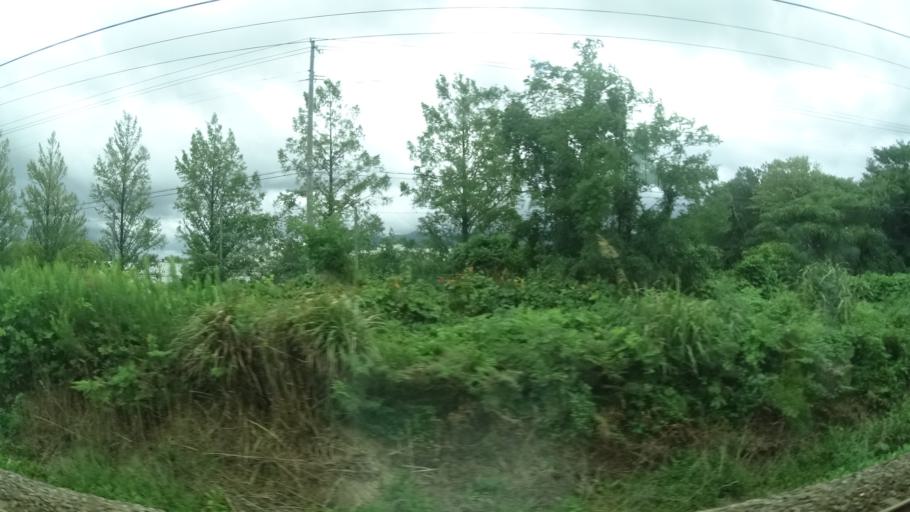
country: JP
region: Niigata
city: Murakami
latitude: 38.1039
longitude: 139.4343
